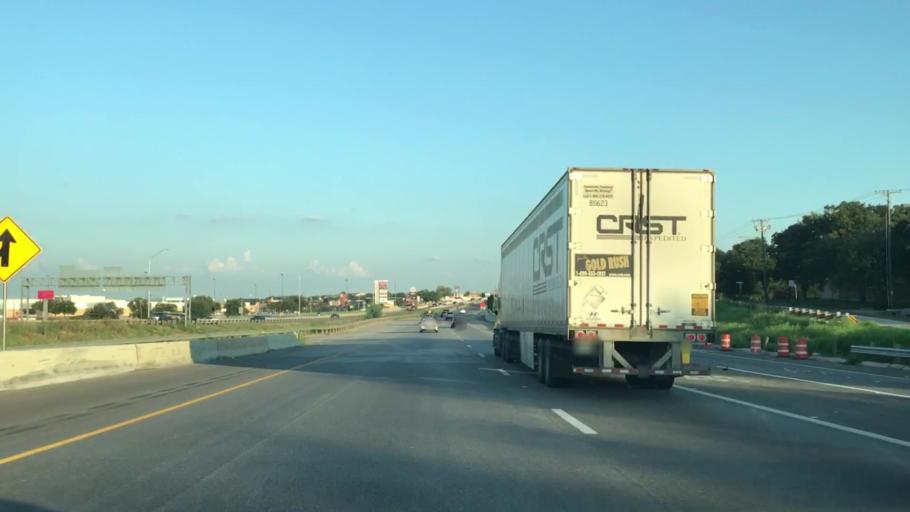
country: US
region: Texas
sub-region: Denton County
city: Denton
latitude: 33.1911
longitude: -97.1148
